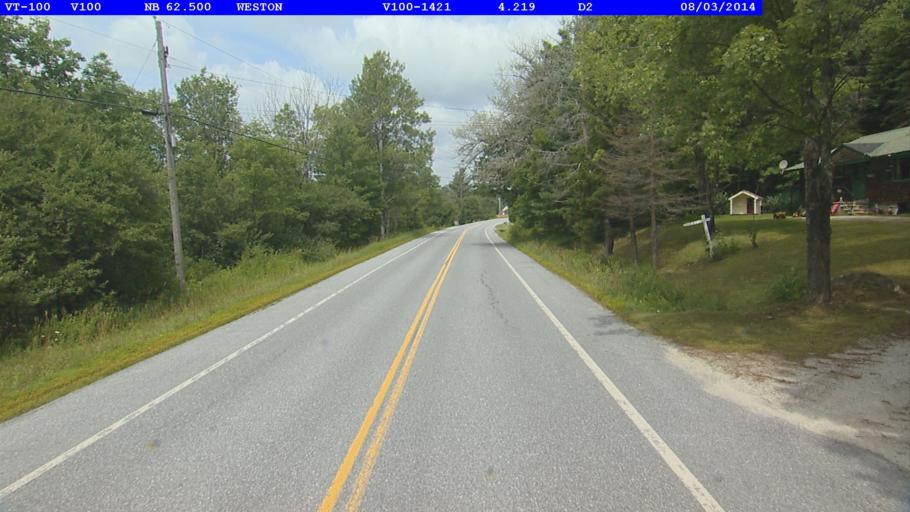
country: US
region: Vermont
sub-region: Windsor County
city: Chester
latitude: 43.3050
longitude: -72.7861
